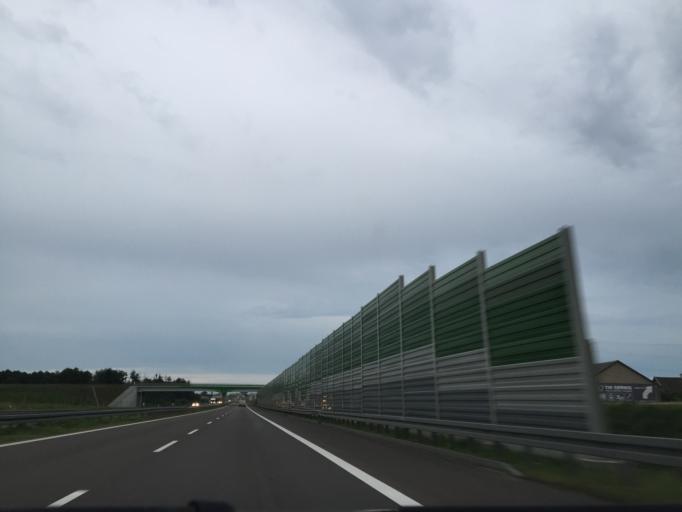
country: PL
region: Podlasie
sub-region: Powiat bialostocki
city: Choroszcz
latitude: 53.1603
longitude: 22.8991
